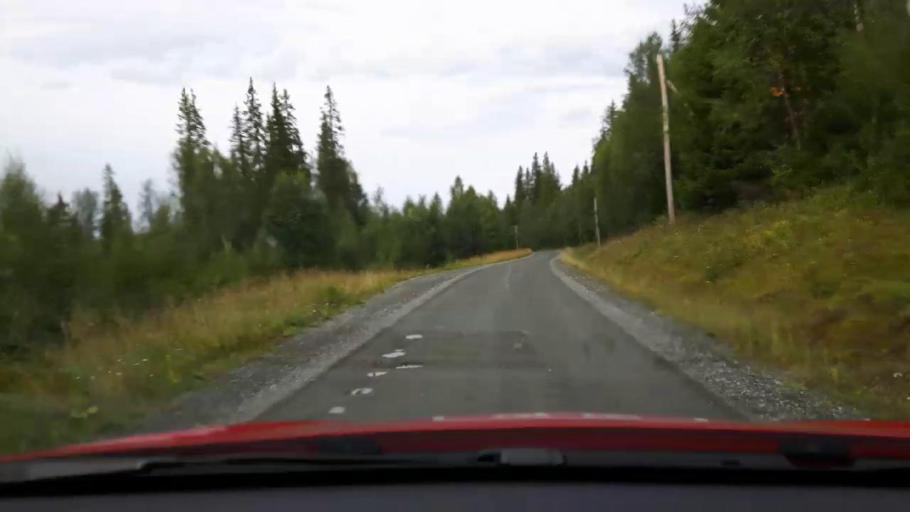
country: SE
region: Jaemtland
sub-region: Are Kommun
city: Are
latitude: 63.7669
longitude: 13.0933
